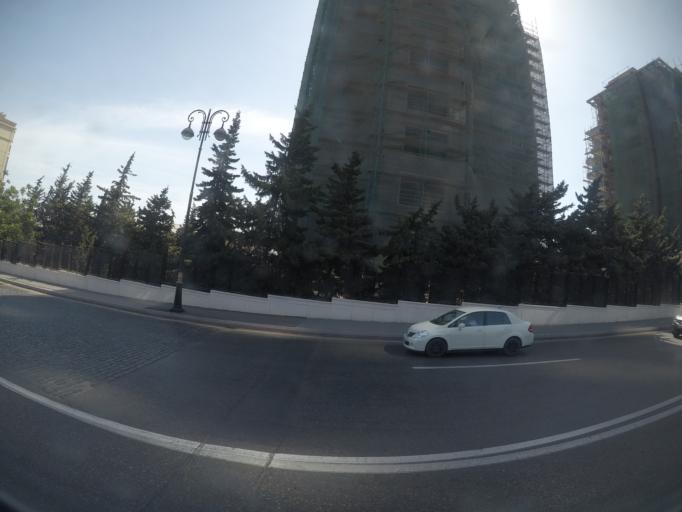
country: AZ
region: Baki
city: Badamdar
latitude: 40.3618
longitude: 49.8267
